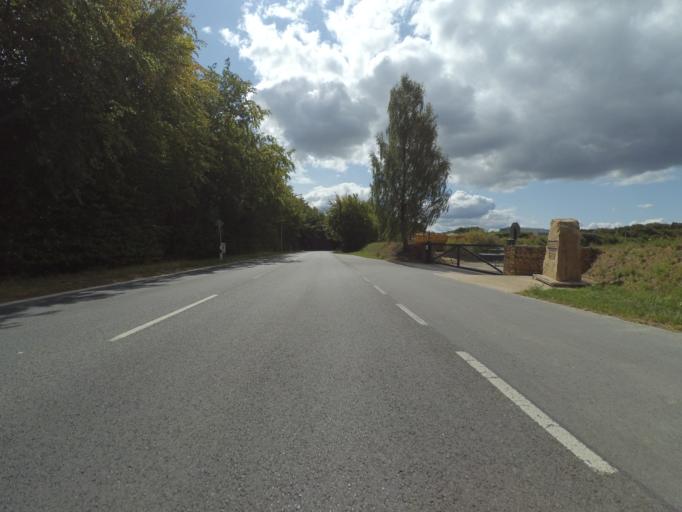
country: LU
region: Luxembourg
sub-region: Canton de Luxembourg
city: Niederanven
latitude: 49.6578
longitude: 6.2264
